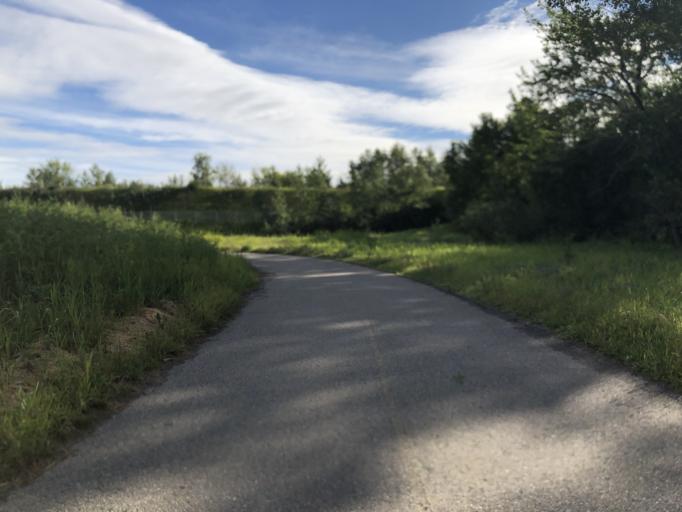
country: CA
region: Alberta
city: Calgary
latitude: 51.0024
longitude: -114.0207
